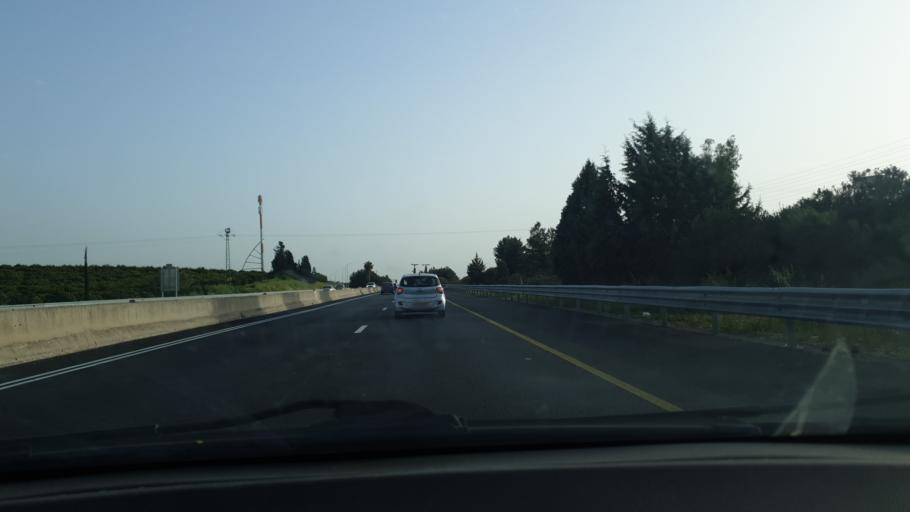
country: IL
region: Central District
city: Even Yehuda
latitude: 32.2398
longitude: 34.8866
